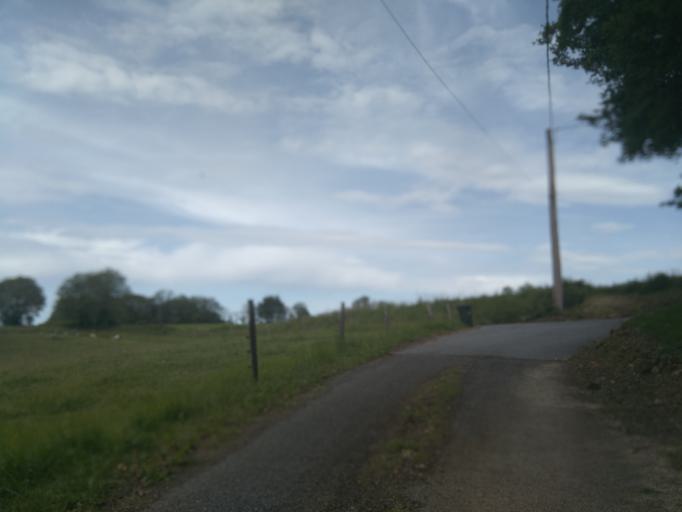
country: FR
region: Aquitaine
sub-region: Departement des Pyrenees-Atlantiques
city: Orthez
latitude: 43.4627
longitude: -0.7696
